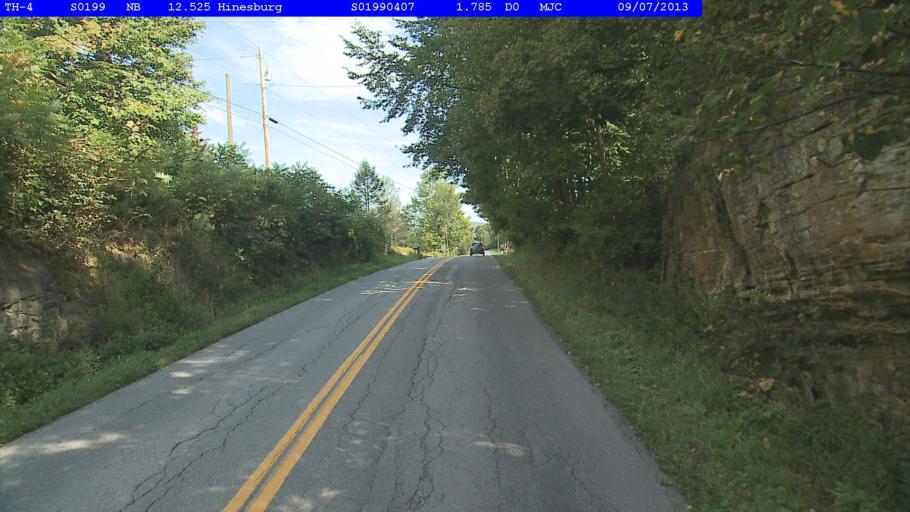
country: US
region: Vermont
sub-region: Chittenden County
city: Hinesburg
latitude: 44.3037
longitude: -73.1092
